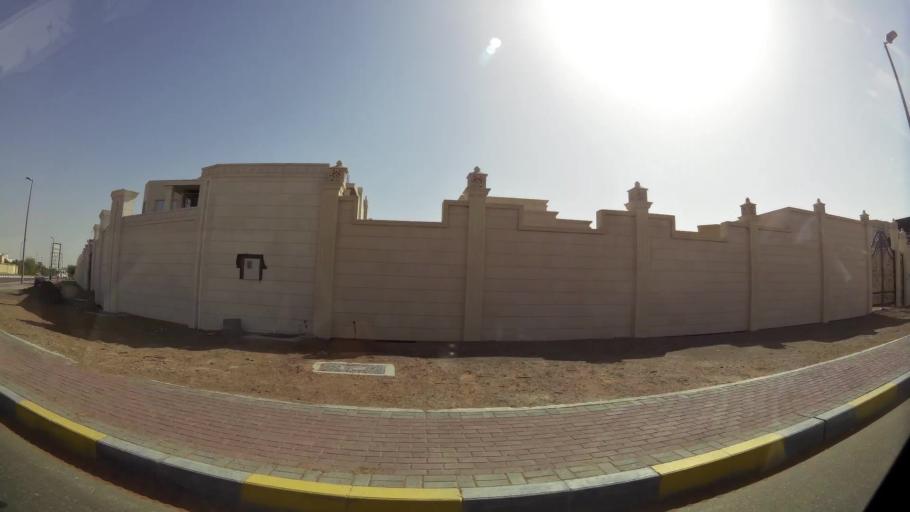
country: OM
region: Al Buraimi
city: Al Buraymi
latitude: 24.3297
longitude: 55.7926
